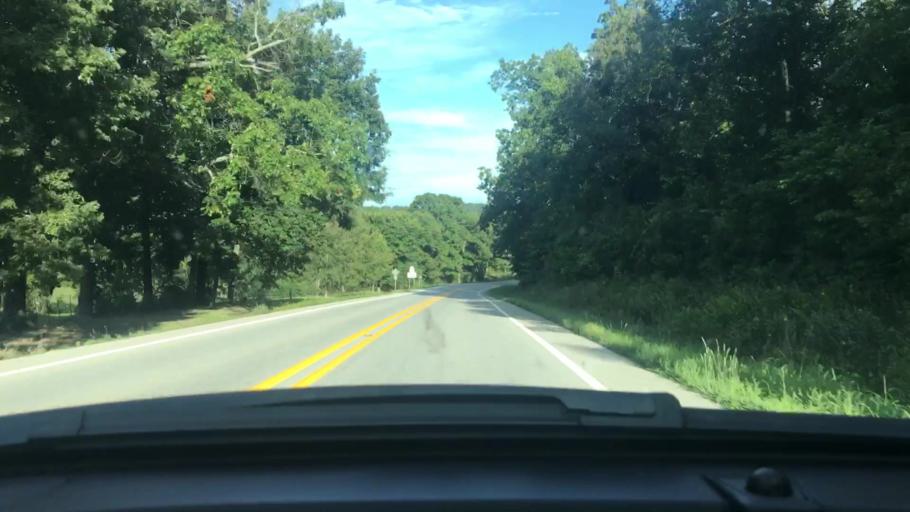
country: US
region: Arkansas
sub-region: Sharp County
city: Cherokee Village
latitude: 36.2742
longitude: -91.3404
